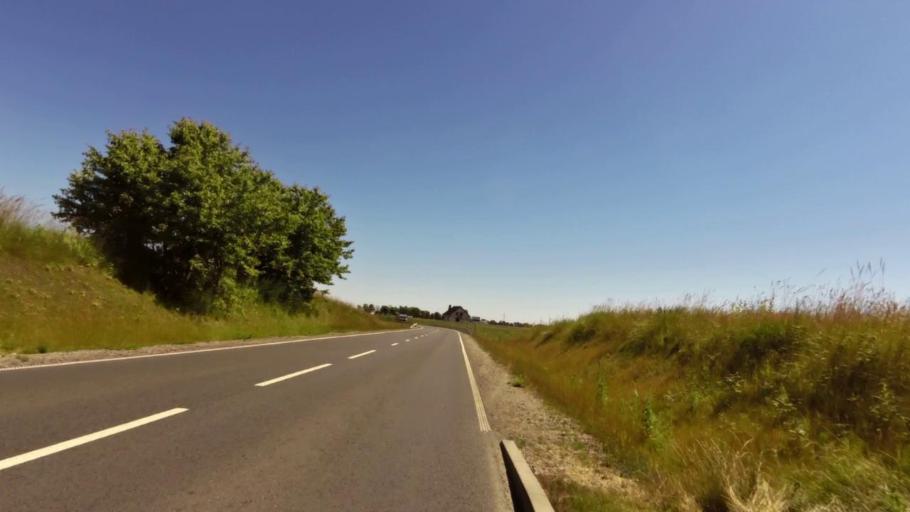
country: PL
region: West Pomeranian Voivodeship
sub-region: Powiat kolobrzeski
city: Goscino
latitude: 54.0450
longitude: 15.6516
